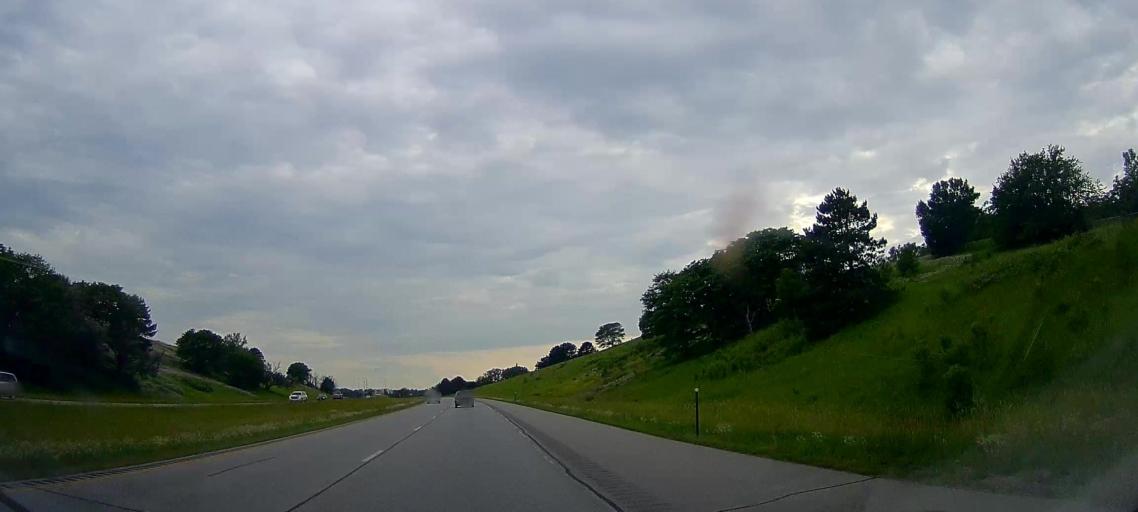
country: US
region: Nebraska
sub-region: Douglas County
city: Bennington
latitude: 41.3313
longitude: -96.0552
